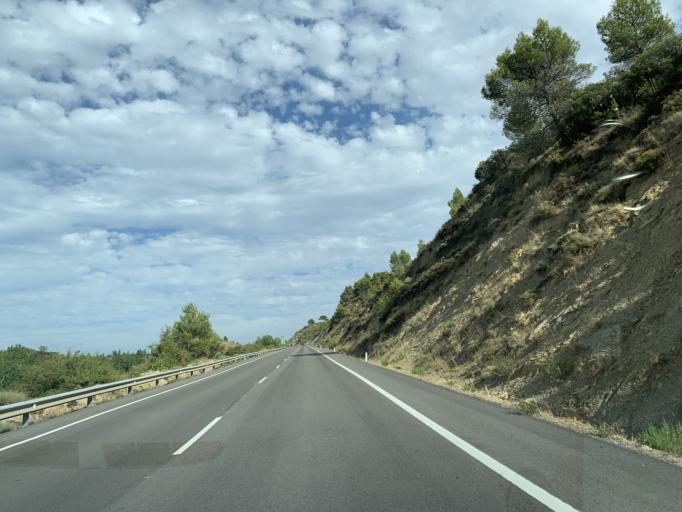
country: ES
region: Aragon
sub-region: Provincia de Zaragoza
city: Santa Eulalia de Gallego
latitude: 42.2930
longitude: -0.7253
